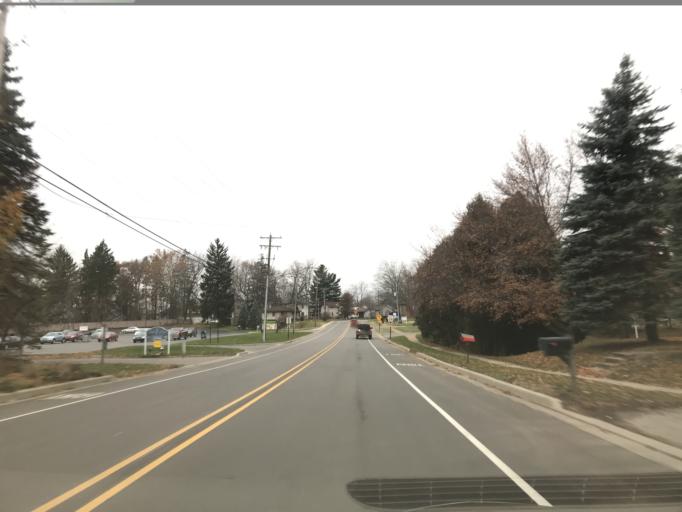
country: US
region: Michigan
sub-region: Eaton County
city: Dimondale
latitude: 42.6474
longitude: -84.6441
